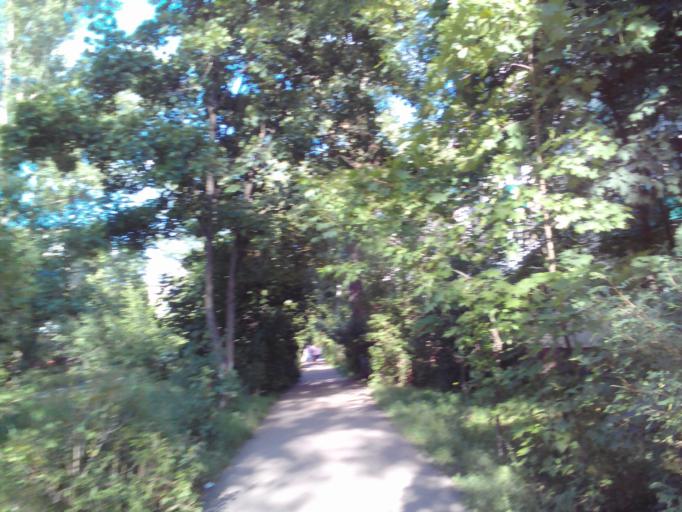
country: RU
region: Kursk
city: Voroshnevo
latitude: 51.6694
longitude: 36.0757
